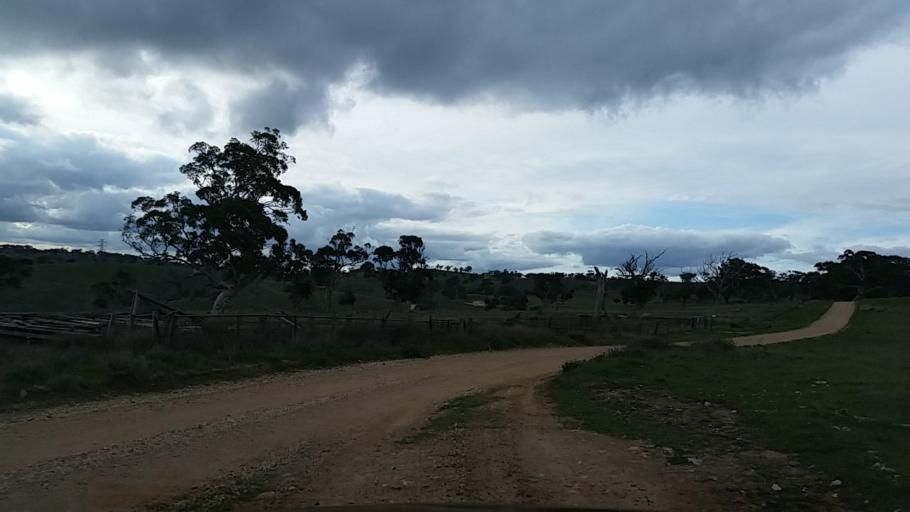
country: AU
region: South Australia
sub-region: Mount Barker
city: Callington
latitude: -34.9613
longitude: 139.0527
